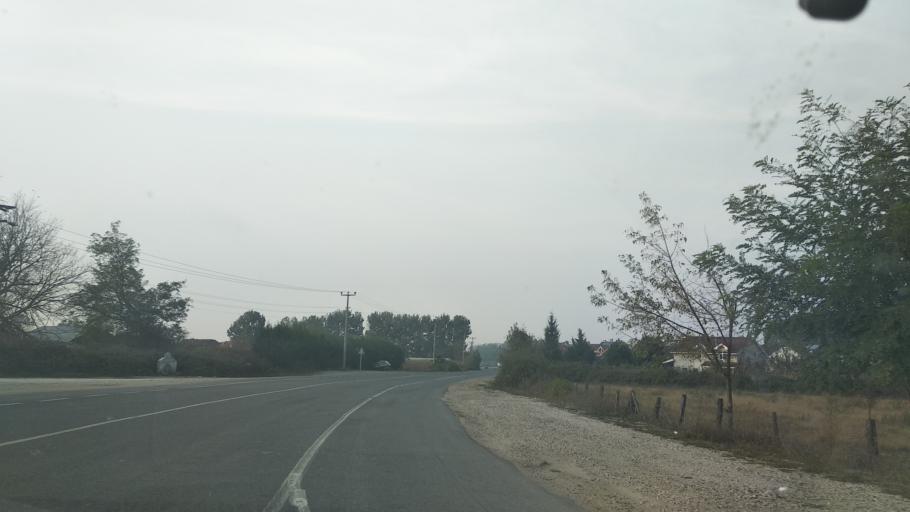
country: TR
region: Duzce
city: Duzce
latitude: 40.8213
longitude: 31.1769
